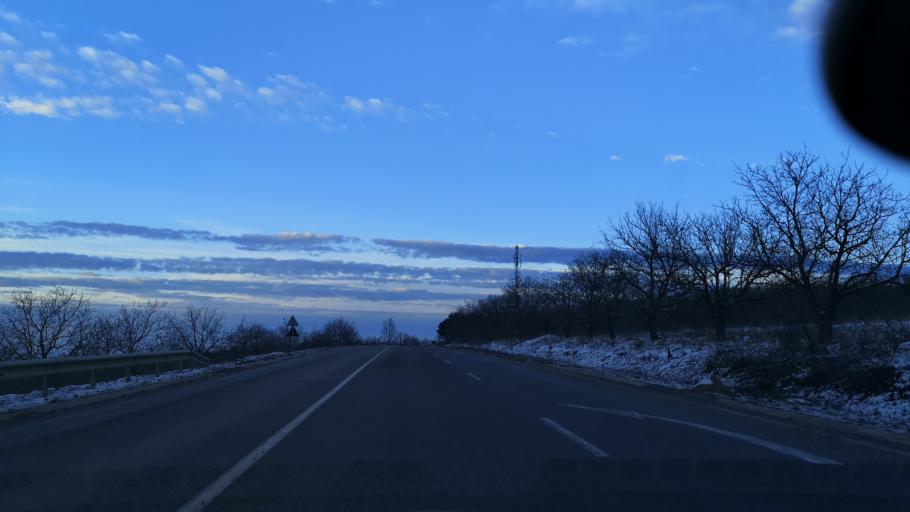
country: MD
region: Orhei
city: Orhei
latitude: 47.5326
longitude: 28.7942
